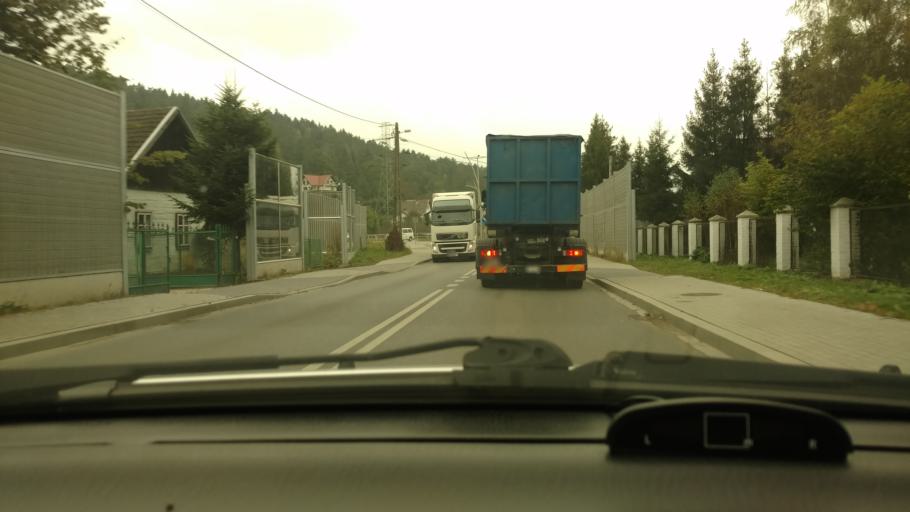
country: PL
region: Lesser Poland Voivodeship
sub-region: Powiat nowosadecki
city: Chelmiec
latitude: 49.6392
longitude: 20.6657
